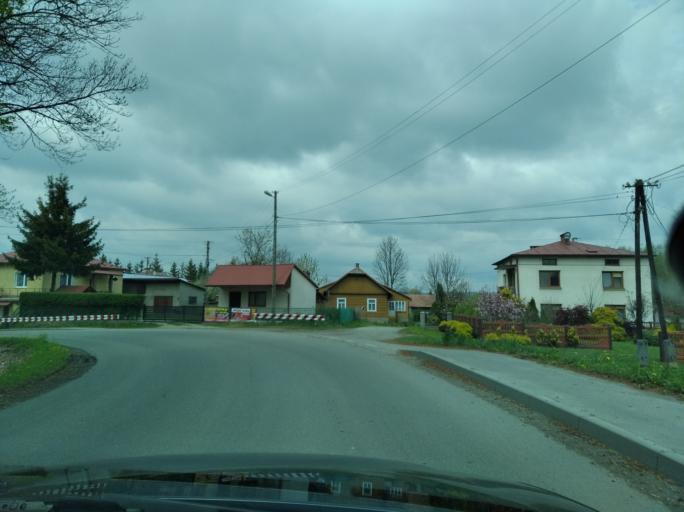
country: PL
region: Subcarpathian Voivodeship
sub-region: Powiat brzozowski
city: Haczow
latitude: 49.6716
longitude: 21.8948
